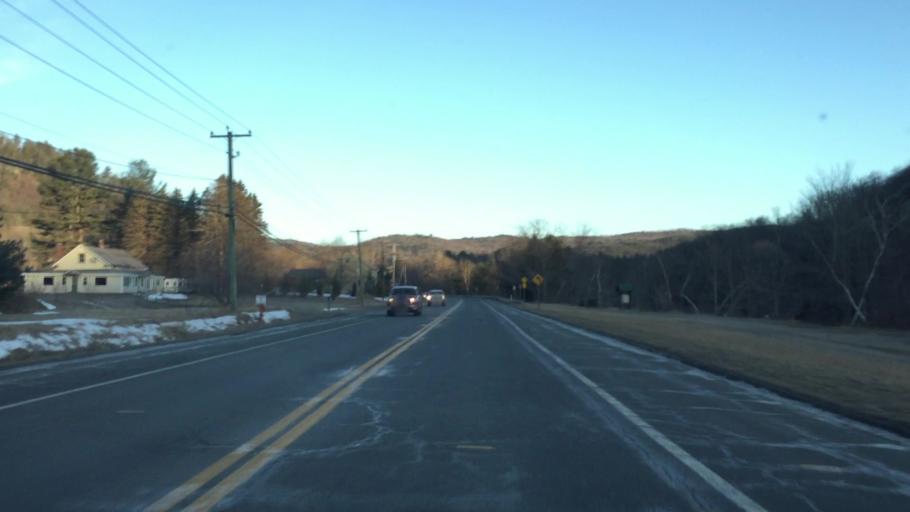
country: US
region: Massachusetts
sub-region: Hampden County
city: Westfield
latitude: 42.1803
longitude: -72.8443
